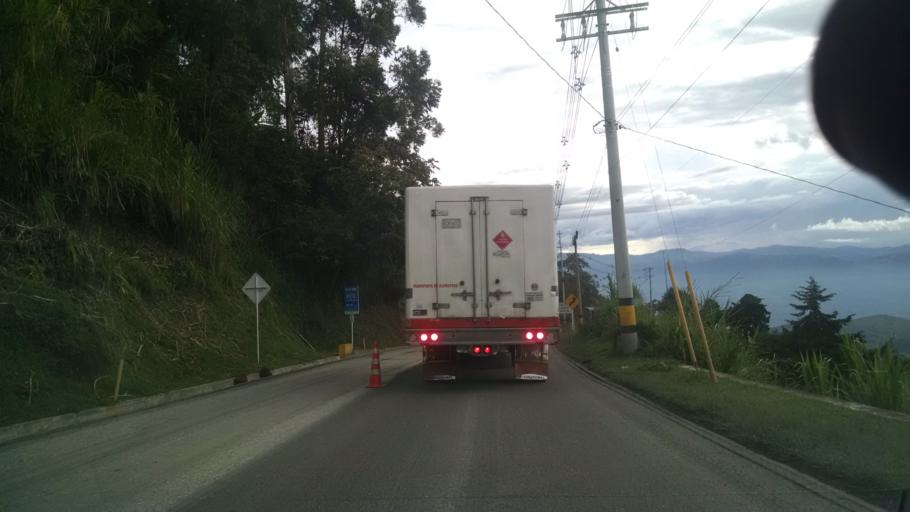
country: CO
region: Antioquia
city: Santa Barbara
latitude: 5.8877
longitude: -75.5719
